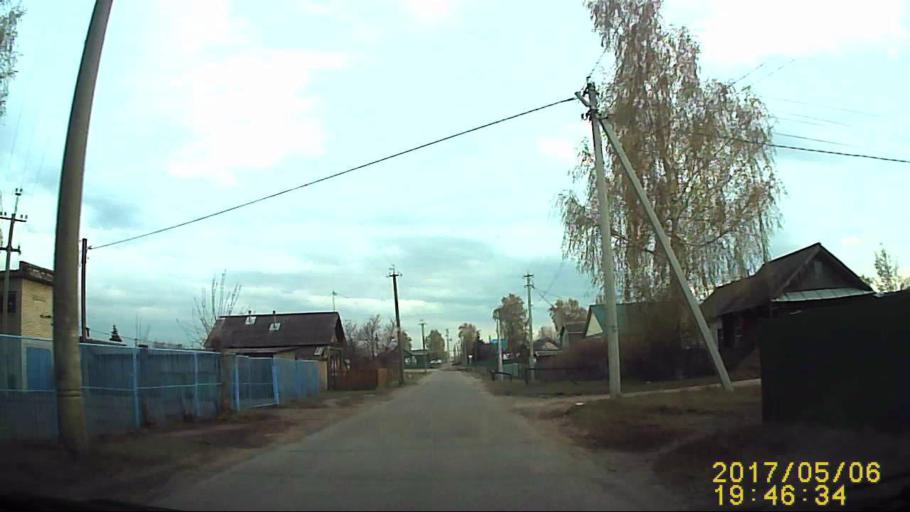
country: RU
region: Ulyanovsk
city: Staraya Mayna
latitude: 54.6052
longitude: 48.9209
